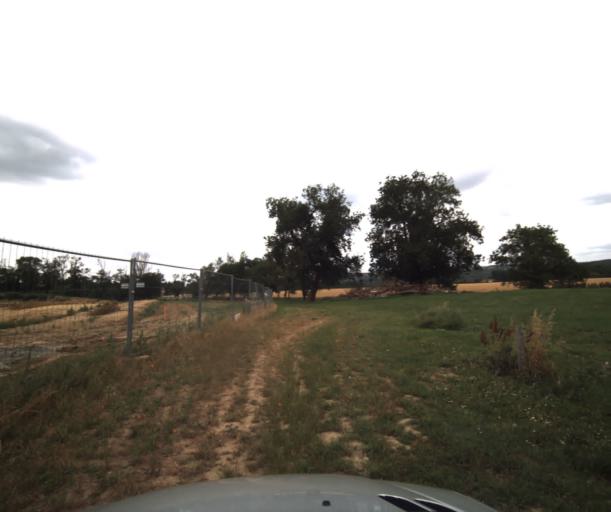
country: FR
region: Midi-Pyrenees
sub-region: Departement de la Haute-Garonne
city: Labarthe-sur-Leze
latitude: 43.4637
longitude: 1.4004
